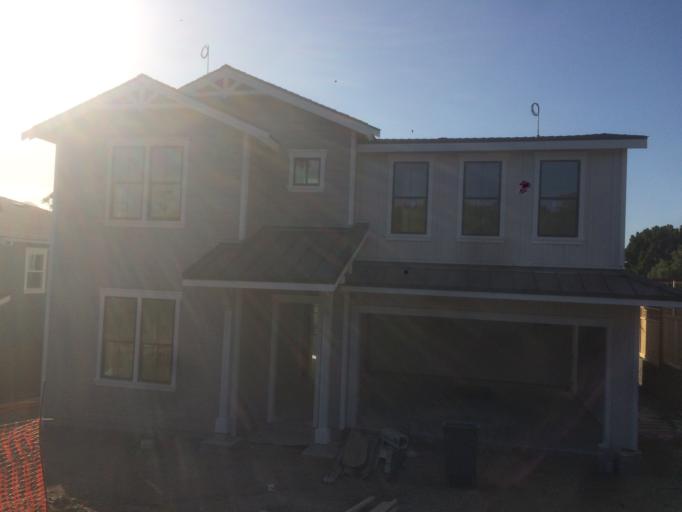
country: US
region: California
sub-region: San Luis Obispo County
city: San Luis Obispo
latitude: 35.2766
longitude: -120.6475
